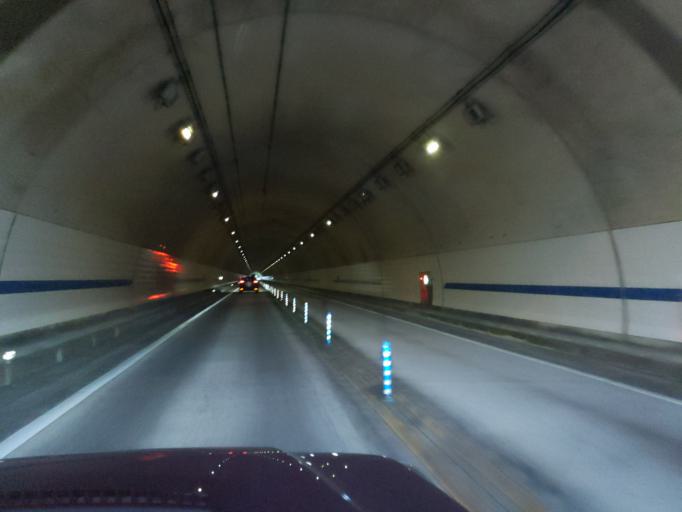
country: JP
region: Tokushima
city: Anan
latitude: 33.7656
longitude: 134.5658
